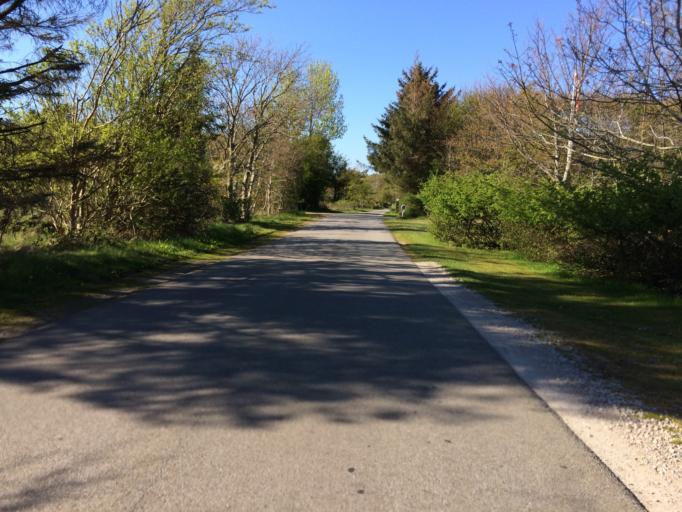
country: DK
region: Central Jutland
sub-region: Struer Kommune
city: Struer
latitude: 56.5471
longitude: 8.6242
